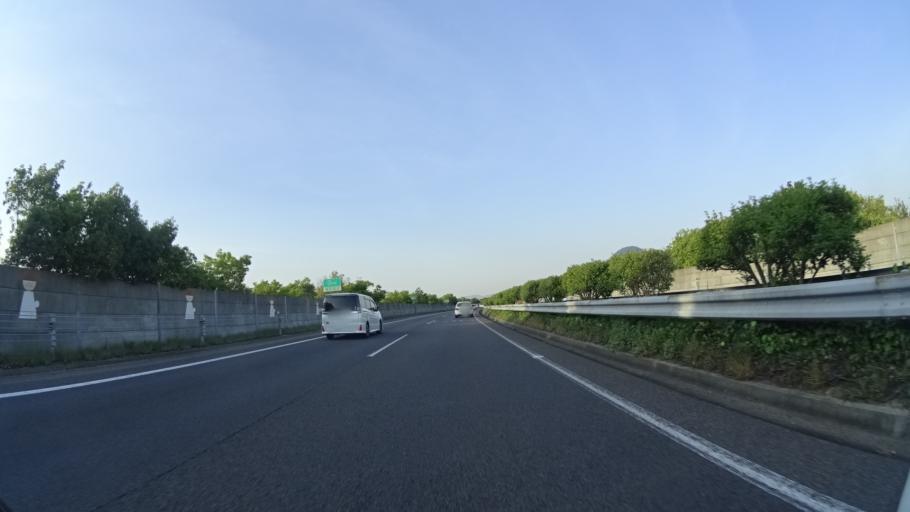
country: JP
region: Kagawa
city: Marugame
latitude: 34.2546
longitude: 133.8050
